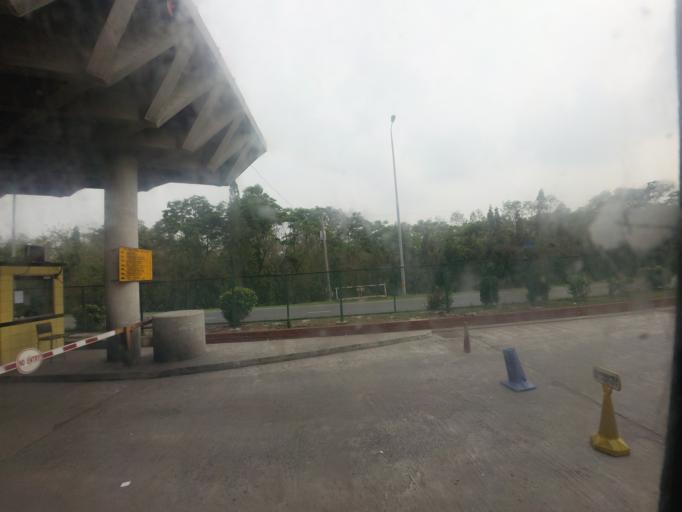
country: BD
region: Rajshahi
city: Sirajganj
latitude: 24.3976
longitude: 89.7480
